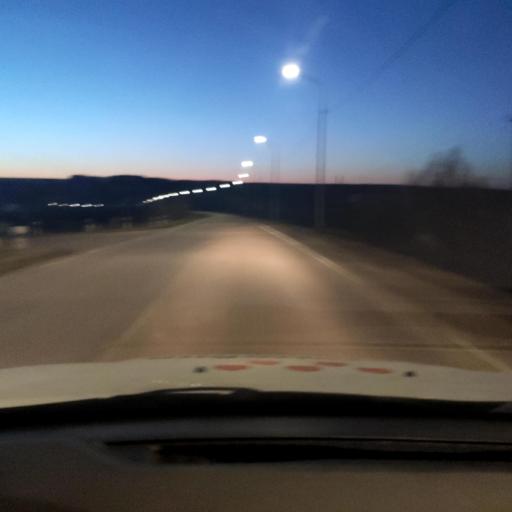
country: RU
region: Bashkortostan
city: Ulukulevo
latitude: 54.5633
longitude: 56.3402
